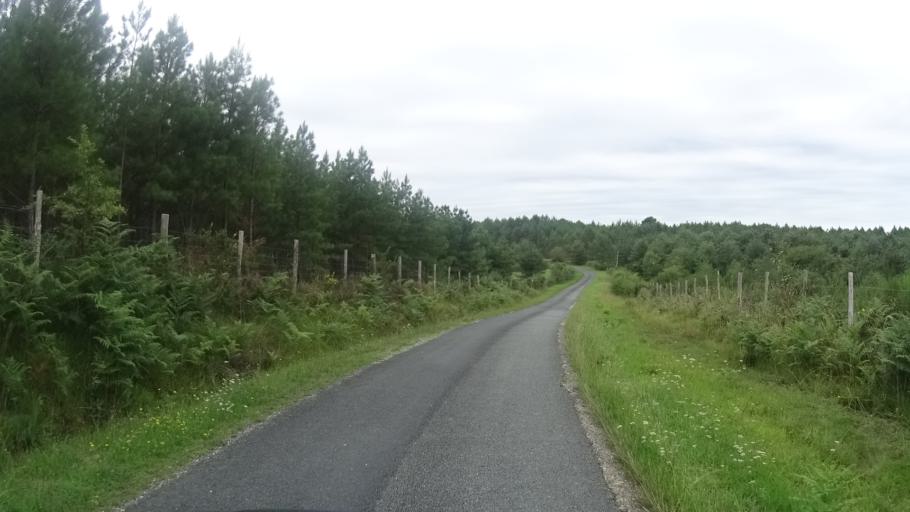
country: FR
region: Aquitaine
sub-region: Departement de la Dordogne
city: Sourzac
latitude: 44.9773
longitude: 0.4633
